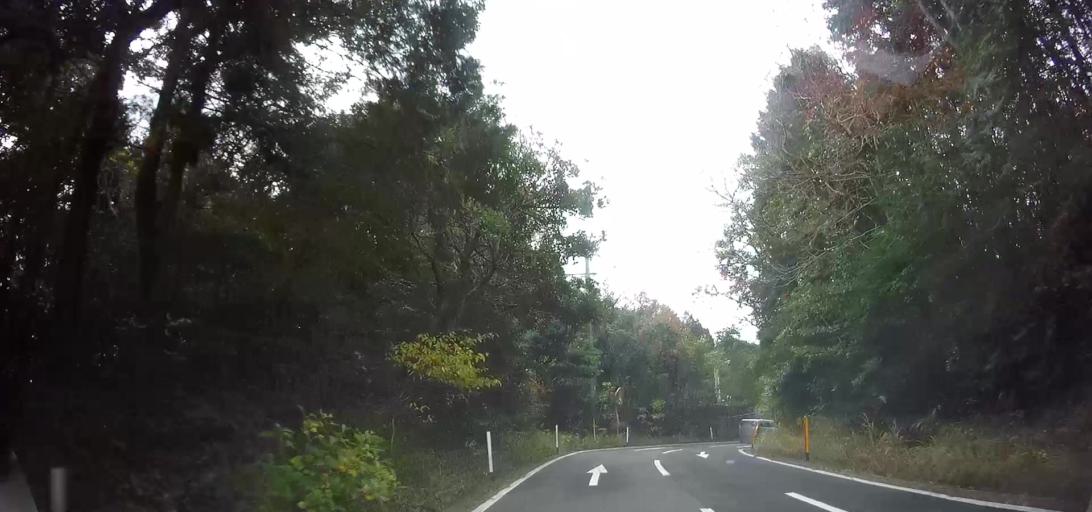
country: JP
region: Nagasaki
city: Shimabara
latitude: 32.7065
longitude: 130.2452
